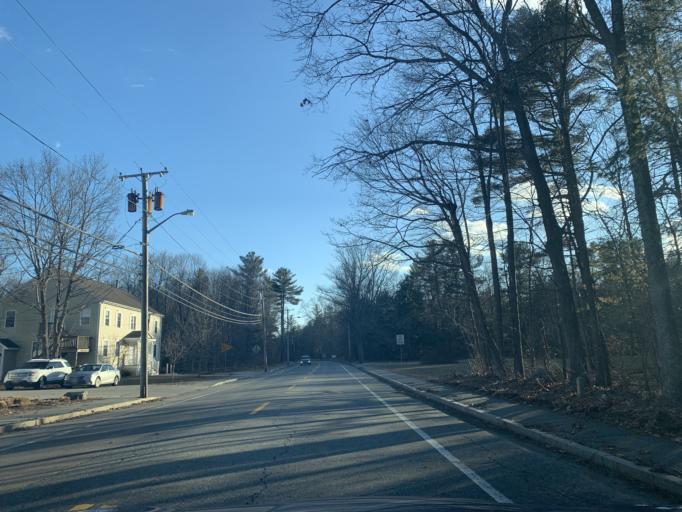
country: US
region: Massachusetts
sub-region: Bristol County
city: Norton
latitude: 41.9644
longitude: -71.1870
